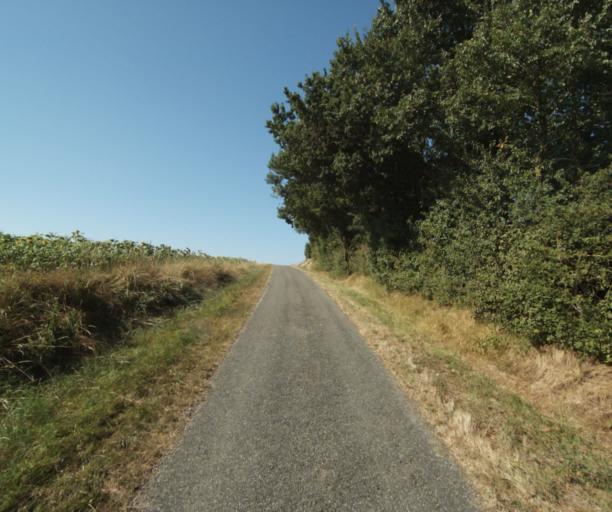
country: FR
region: Midi-Pyrenees
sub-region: Departement de la Haute-Garonne
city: Saint-Felix-Lauragais
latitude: 43.5051
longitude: 1.9205
